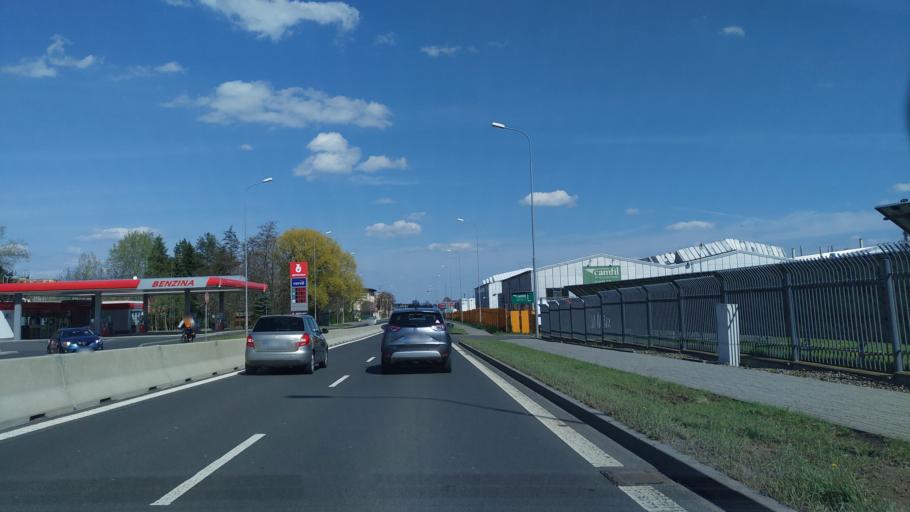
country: CZ
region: Ustecky
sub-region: Okres Chomutov
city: Chomutov
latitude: 50.4578
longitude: 13.3874
